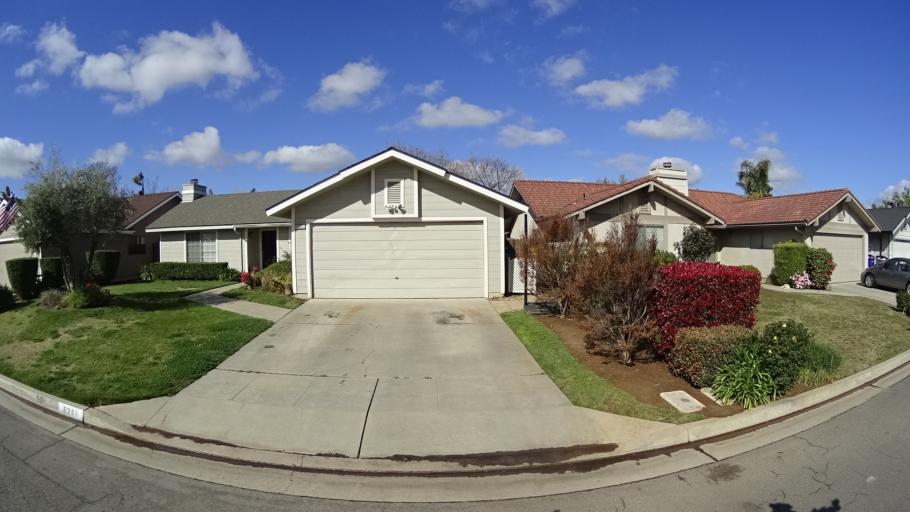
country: US
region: California
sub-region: Fresno County
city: West Park
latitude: 36.8287
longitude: -119.8797
